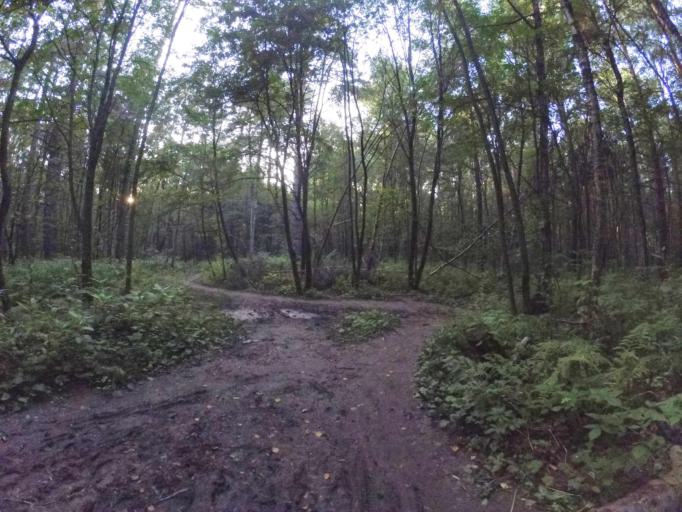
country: RU
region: Moscow
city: Khimki
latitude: 55.8737
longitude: 37.4271
